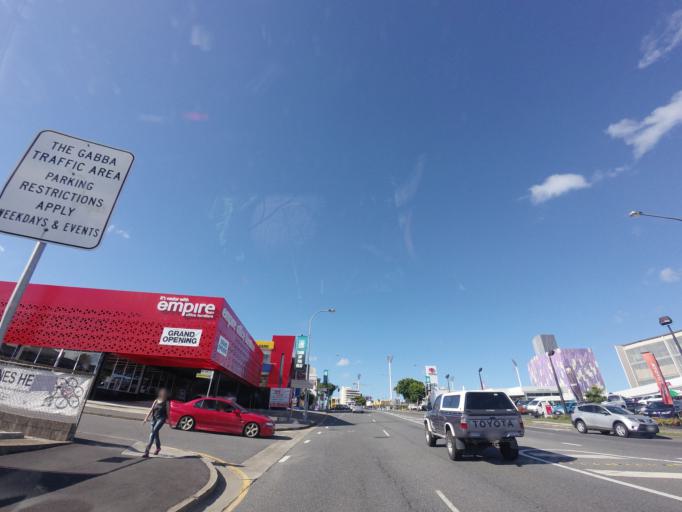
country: AU
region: Queensland
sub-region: Brisbane
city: Woolloongabba
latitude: -27.4896
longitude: 153.0356
